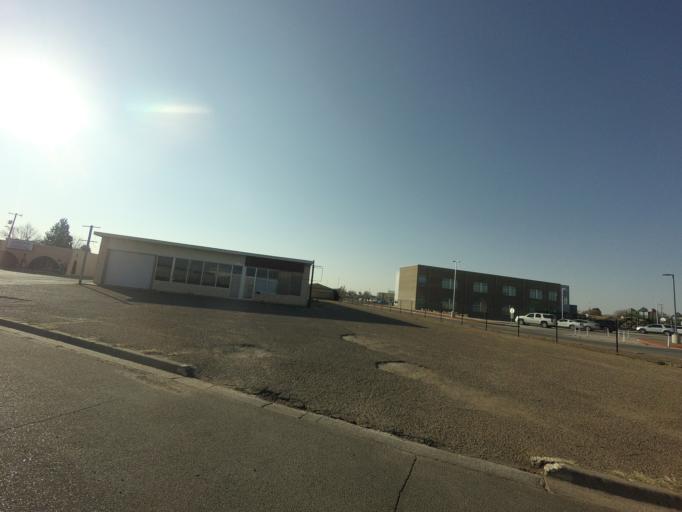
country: US
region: New Mexico
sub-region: Curry County
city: Clovis
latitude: 34.4147
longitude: -103.2096
